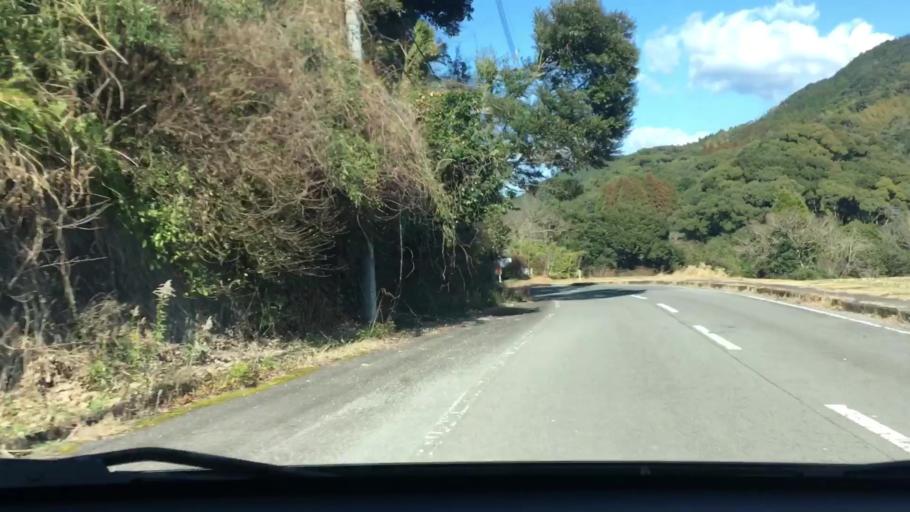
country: JP
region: Kagoshima
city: Ijuin
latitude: 31.7431
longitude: 130.4095
